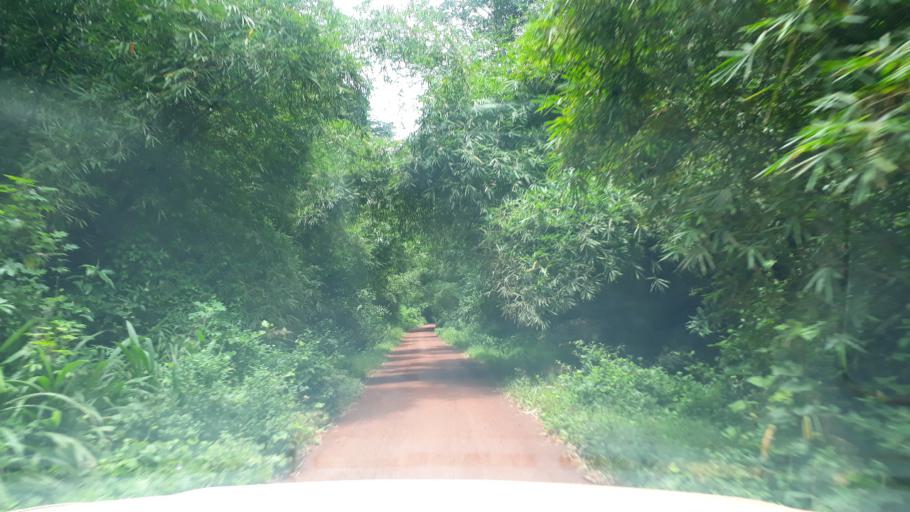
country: CD
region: Eastern Province
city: Aketi
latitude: 2.9176
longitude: 24.0652
